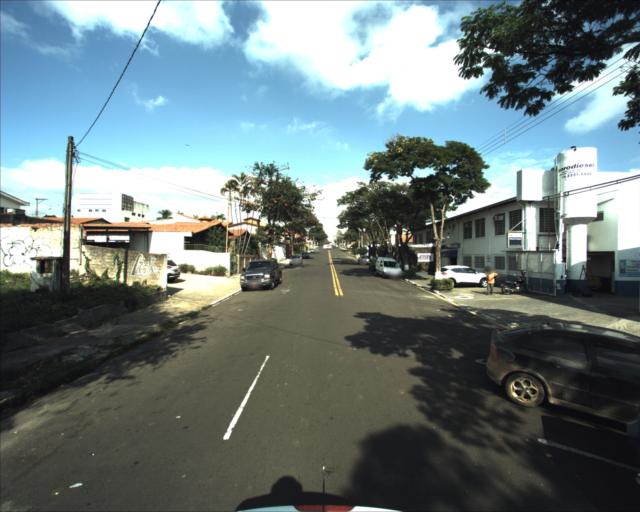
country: BR
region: Sao Paulo
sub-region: Sorocaba
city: Sorocaba
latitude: -23.4818
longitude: -47.4397
